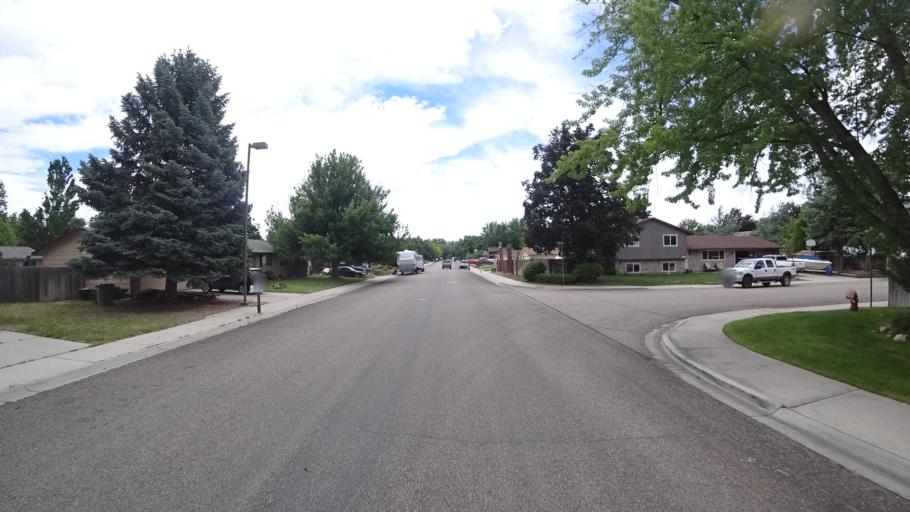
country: US
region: Idaho
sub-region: Ada County
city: Eagle
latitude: 43.6373
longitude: -116.3244
